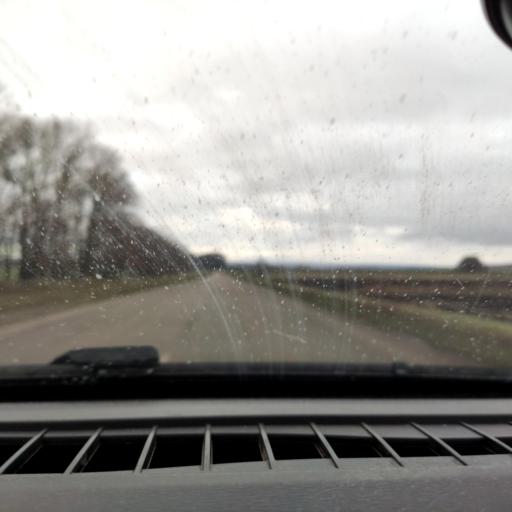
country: RU
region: Belgorod
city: Ilovka
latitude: 50.7361
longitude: 38.7032
